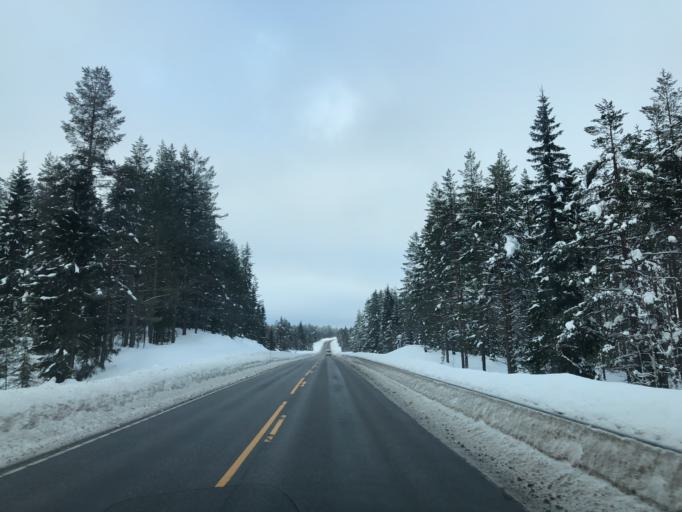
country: NO
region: Hedmark
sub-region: Trysil
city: Innbygda
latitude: 61.2273
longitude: 12.2488
